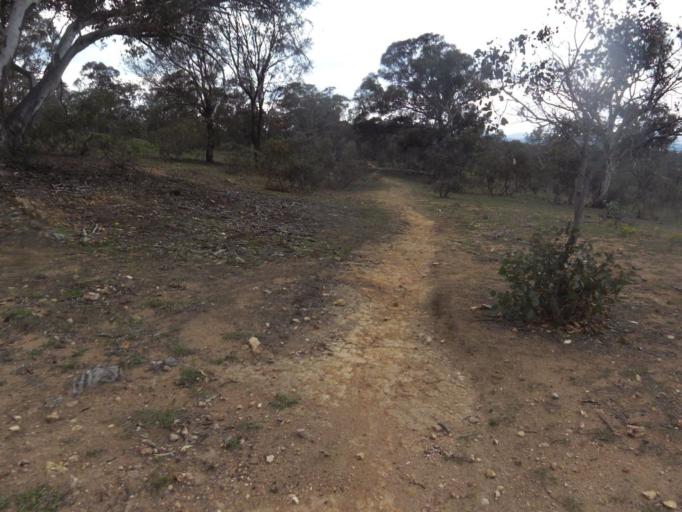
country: AU
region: Australian Capital Territory
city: Forrest
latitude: -35.3473
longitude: 149.1345
